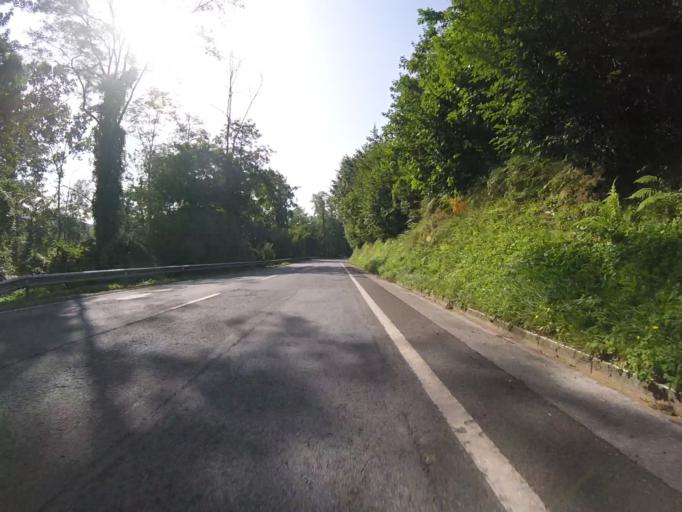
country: ES
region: Navarre
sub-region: Provincia de Navarra
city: Zugarramurdi
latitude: 43.2026
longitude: -1.4854
